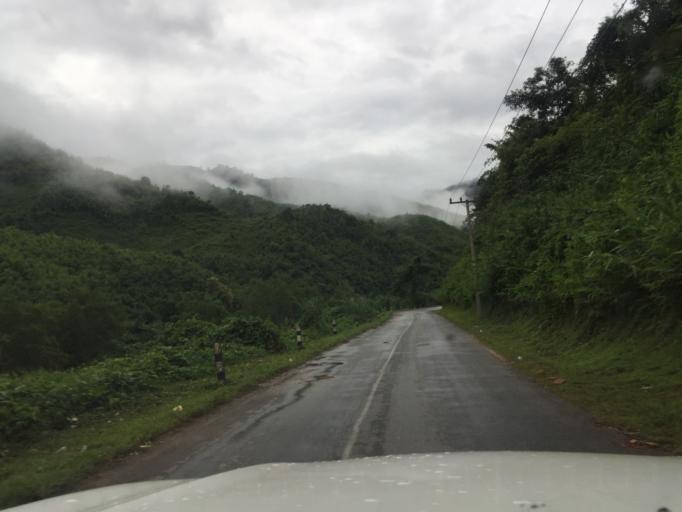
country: LA
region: Oudomxai
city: Muang La
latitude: 20.9321
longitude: 102.2065
